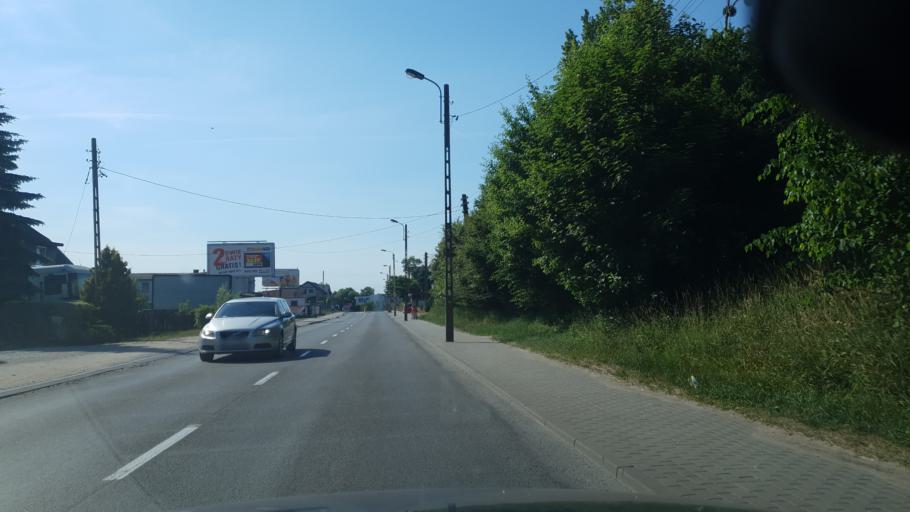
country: PL
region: Pomeranian Voivodeship
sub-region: Gdynia
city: Wielki Kack
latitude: 54.4389
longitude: 18.4599
